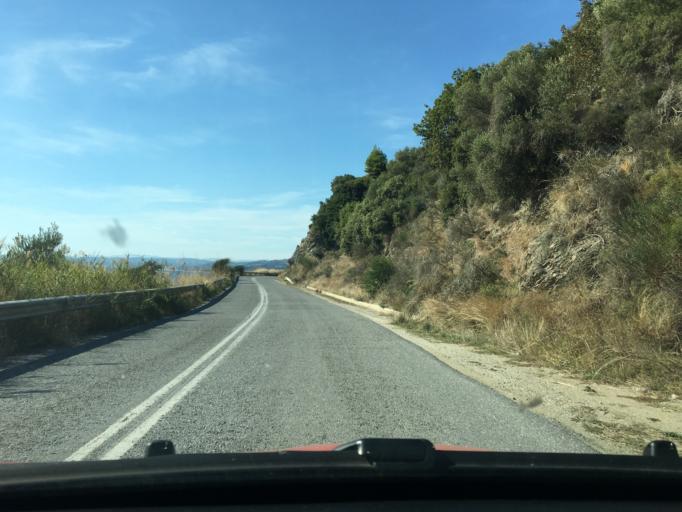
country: GR
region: Central Macedonia
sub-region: Nomos Chalkidikis
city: Nea Roda
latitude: 40.3569
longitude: 23.9427
